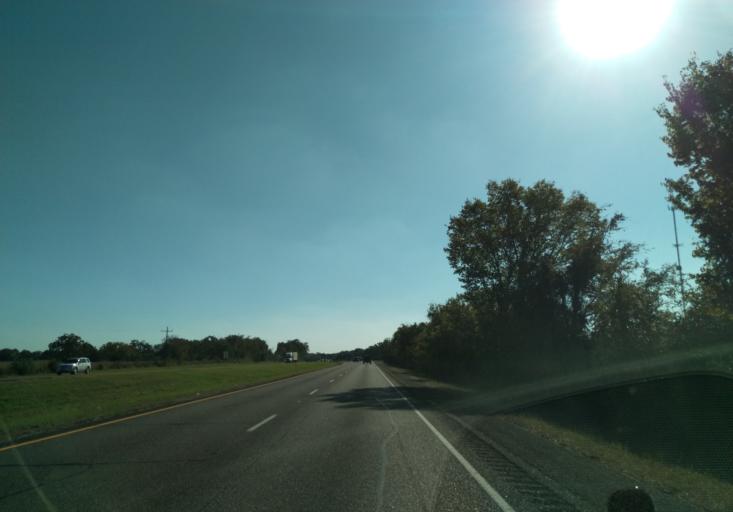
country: US
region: Texas
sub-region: Waller County
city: Hempstead
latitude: 30.2358
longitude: -96.0527
